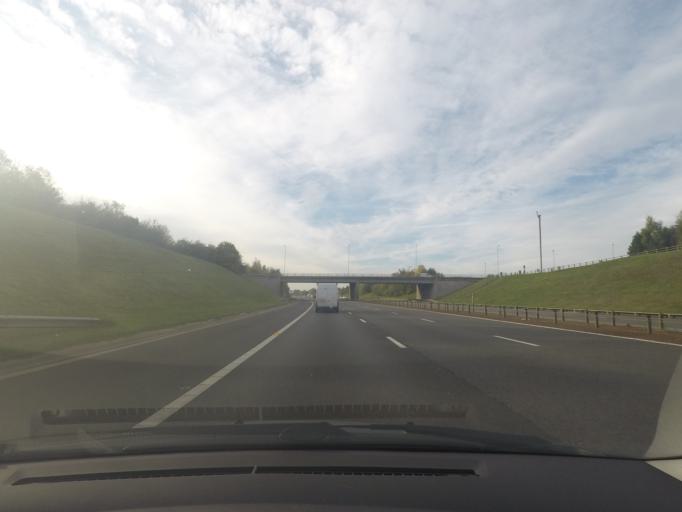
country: GB
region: England
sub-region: City and Borough of Leeds
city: Swillington
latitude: 53.7924
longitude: -1.4261
